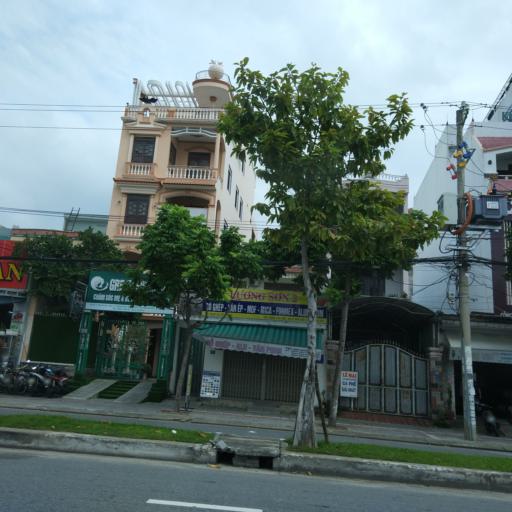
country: VN
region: Da Nang
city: Son Tra
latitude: 16.0699
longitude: 108.2317
